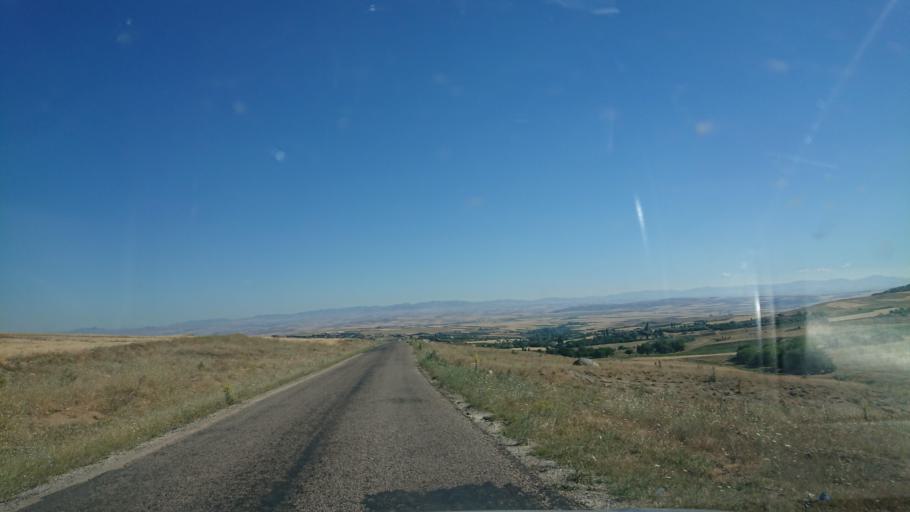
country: TR
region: Aksaray
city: Agacoren
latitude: 38.8412
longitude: 33.9524
